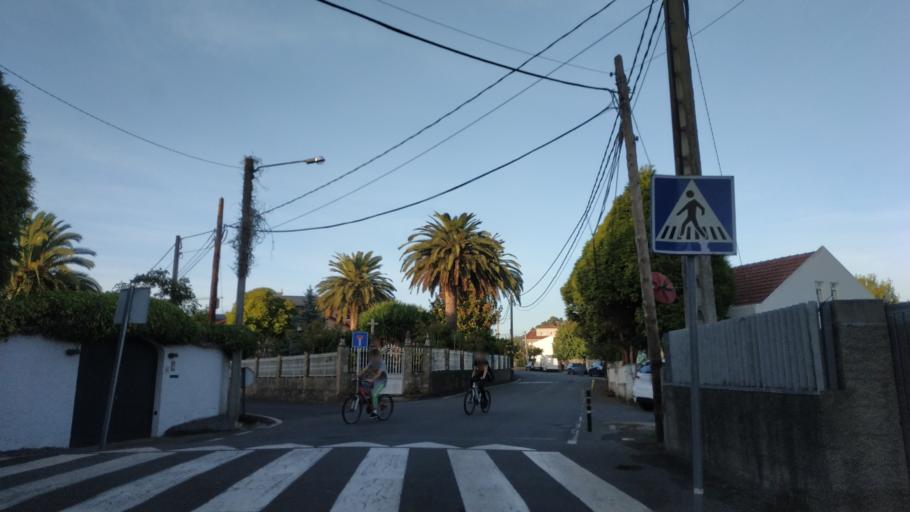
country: ES
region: Galicia
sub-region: Provincia da Coruna
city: Oleiros
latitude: 43.3538
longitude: -8.3446
